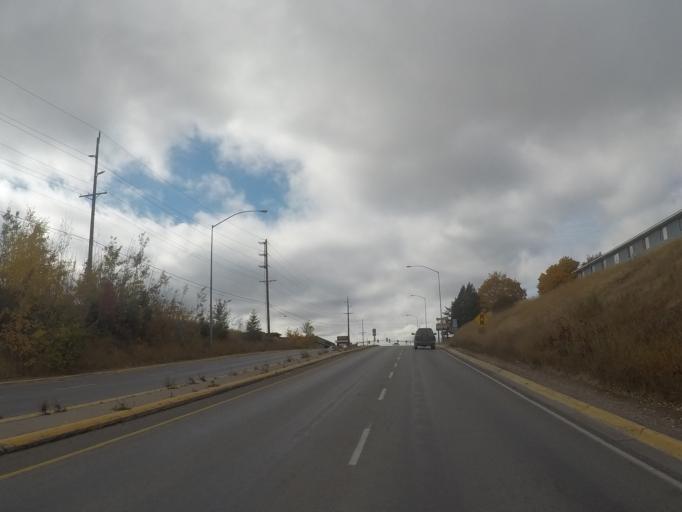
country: US
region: Montana
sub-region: Flathead County
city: Kalispell
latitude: 48.2047
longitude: -114.2994
